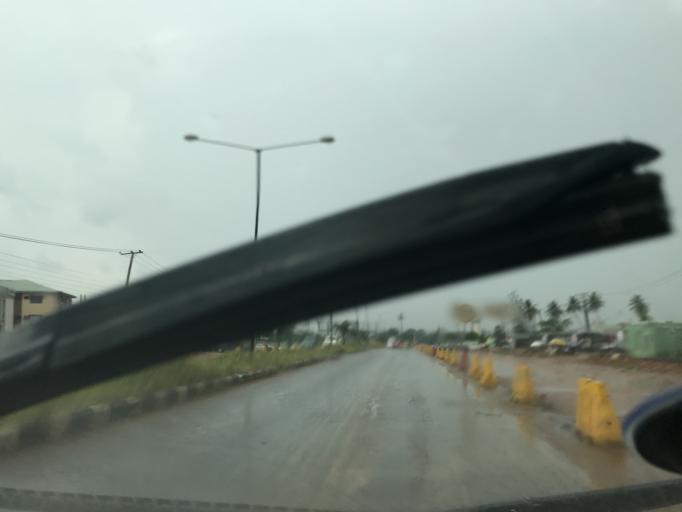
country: NG
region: Lagos
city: Oshodi
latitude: 6.5529
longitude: 3.3276
